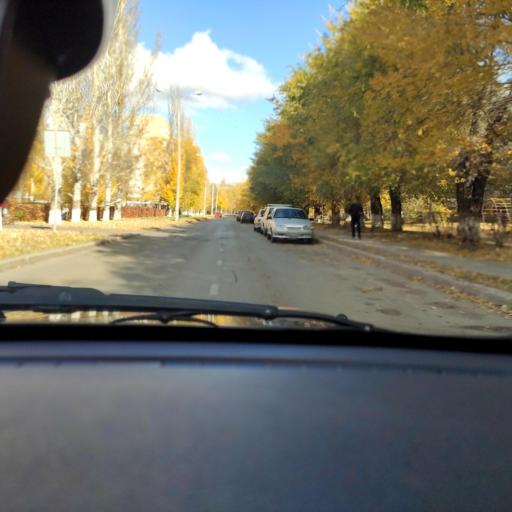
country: RU
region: Samara
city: Tol'yatti
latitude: 53.5315
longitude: 49.2925
